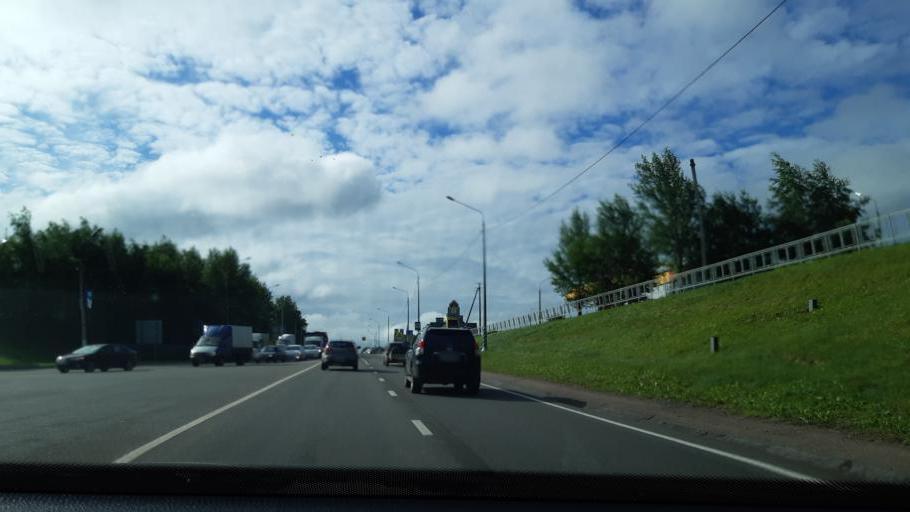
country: RU
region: Smolensk
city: Smolensk
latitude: 54.7563
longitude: 32.0717
